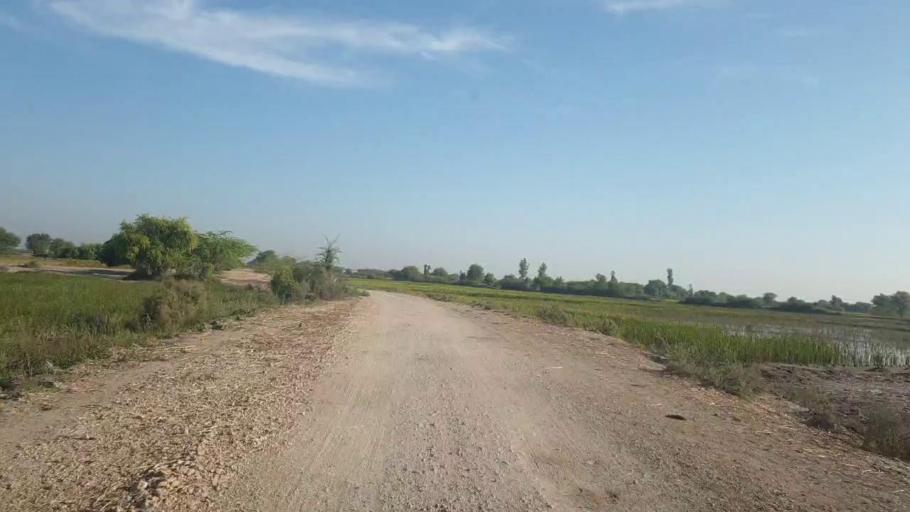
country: PK
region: Sindh
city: Talhar
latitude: 24.8224
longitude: 68.8393
